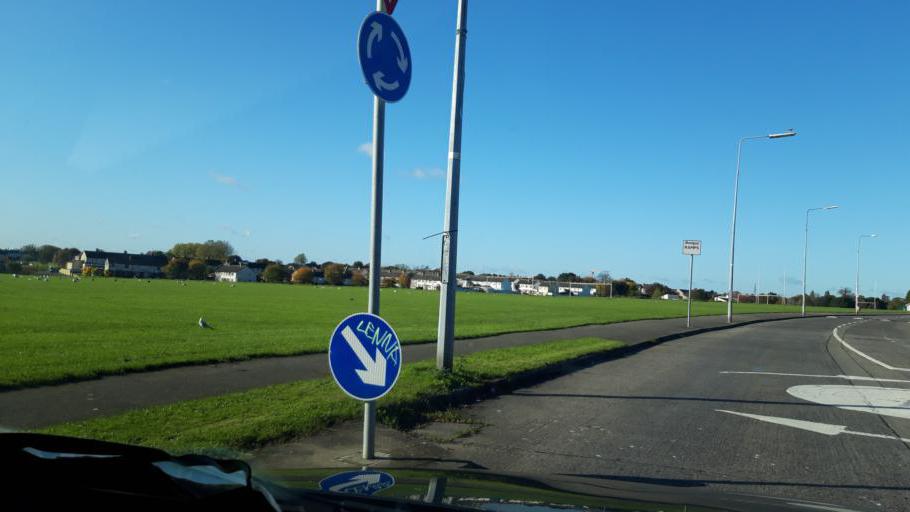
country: IE
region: Leinster
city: Raheny
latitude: 53.3841
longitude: -6.1842
